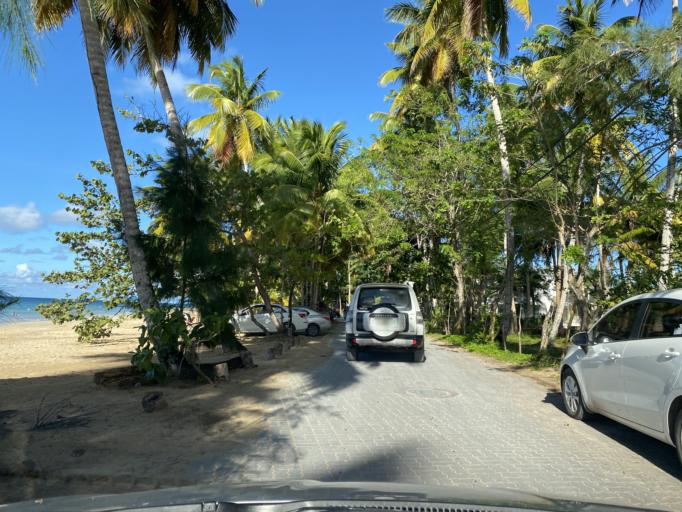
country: DO
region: Samana
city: Las Terrenas
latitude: 19.3196
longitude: -69.5560
